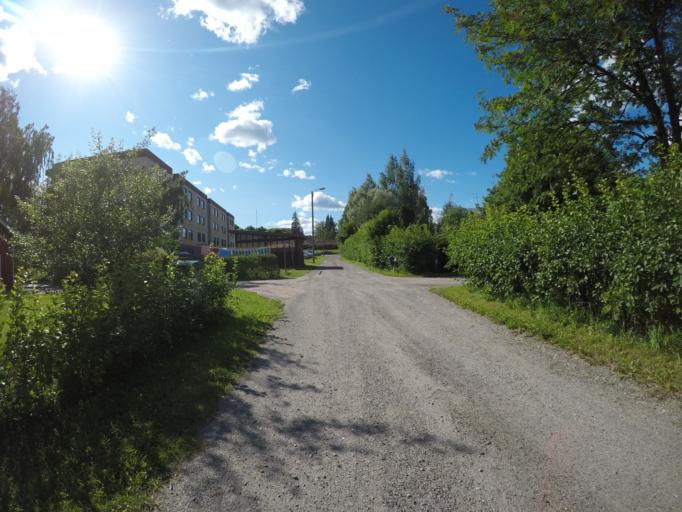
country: FI
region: Haeme
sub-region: Haemeenlinna
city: Haemeenlinna
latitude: 61.0040
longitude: 24.5021
